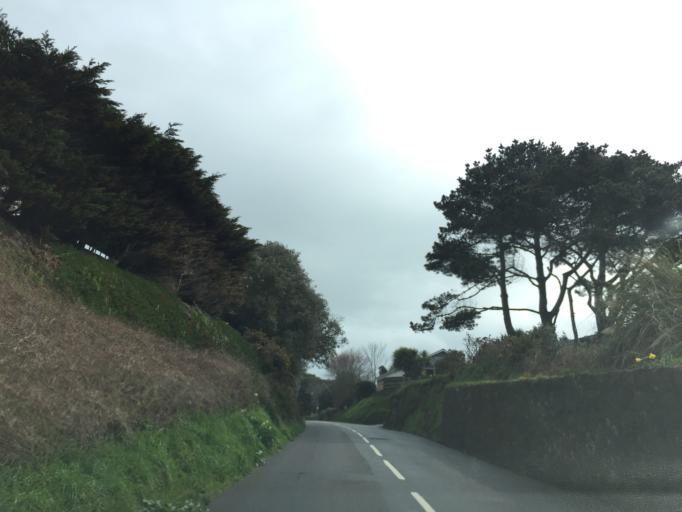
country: JE
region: St Helier
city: Saint Helier
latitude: 49.1844
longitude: -2.2287
